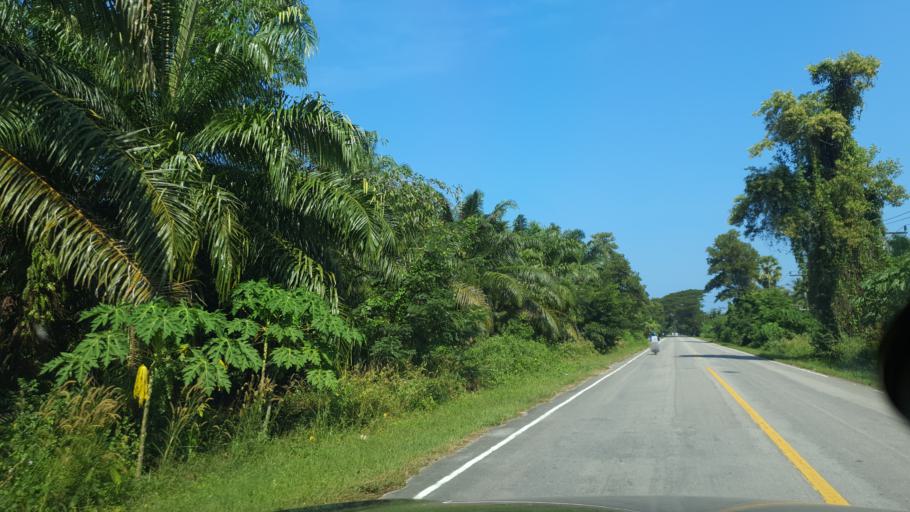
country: TH
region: Surat Thani
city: Tha Chana
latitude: 9.5806
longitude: 99.1920
